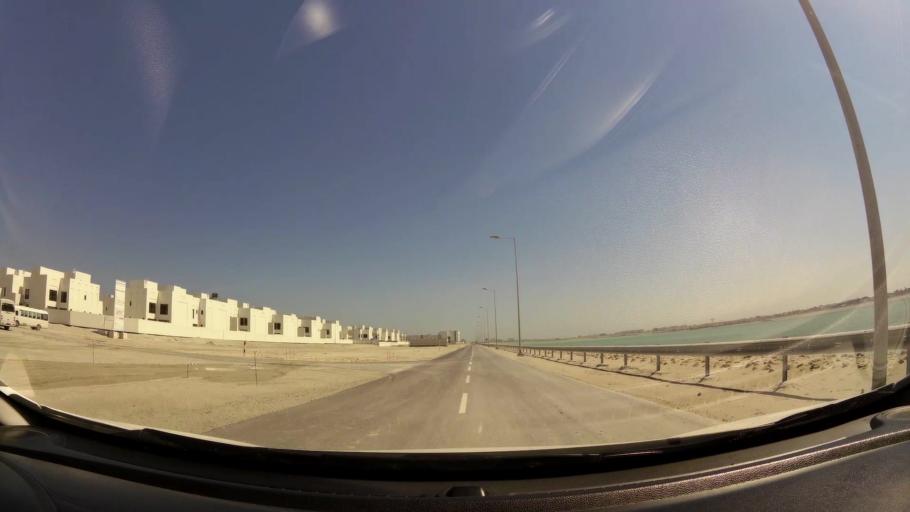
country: BH
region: Muharraq
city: Al Muharraq
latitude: 26.3006
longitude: 50.6315
